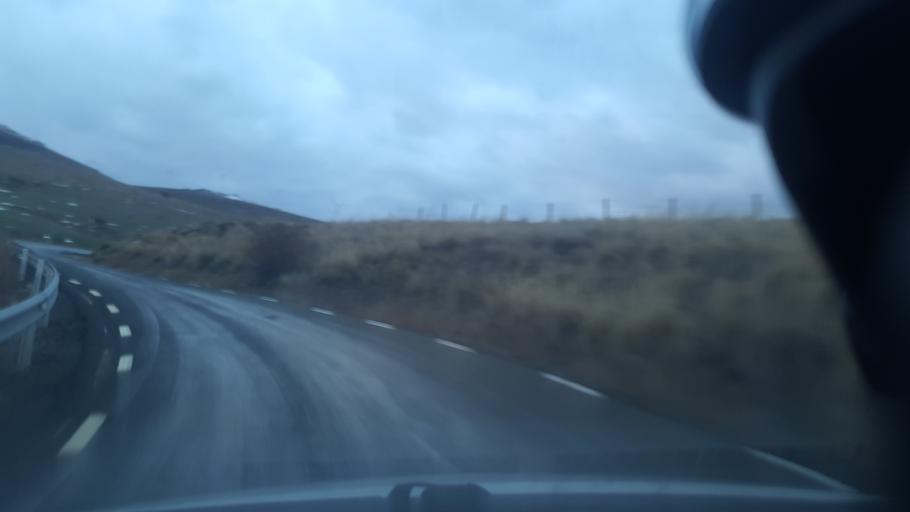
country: ES
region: Castille and Leon
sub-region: Provincia de Avila
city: Ojos-Albos
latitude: 40.7029
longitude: -4.4466
